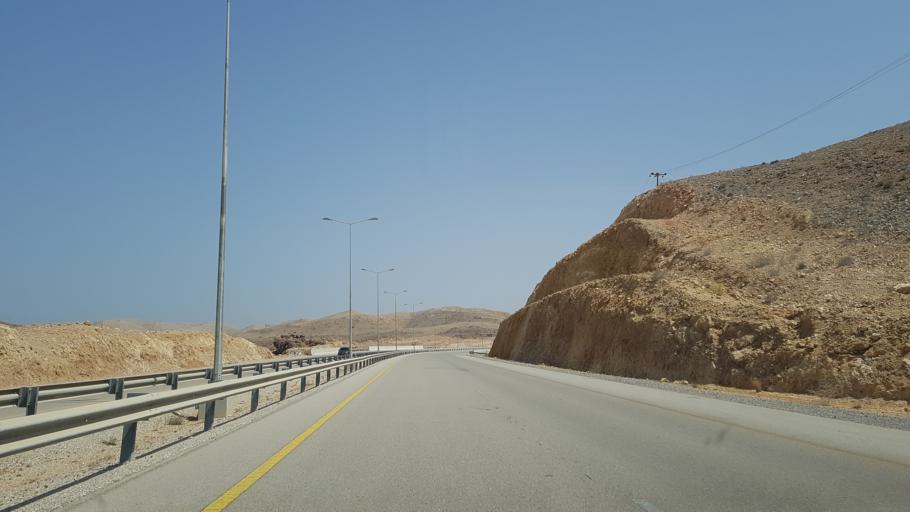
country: OM
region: Muhafazat Masqat
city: Muscat
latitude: 23.1384
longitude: 58.9695
